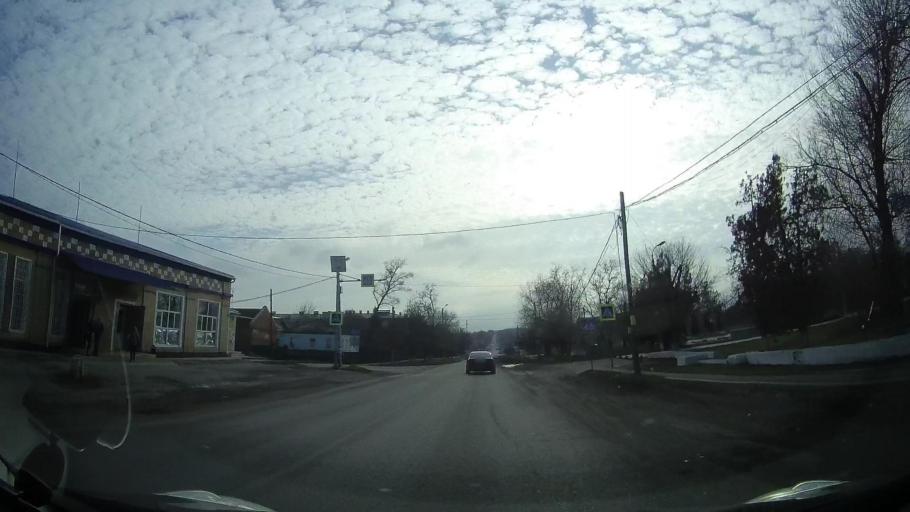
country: RU
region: Rostov
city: Mechetinskaya
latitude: 46.7671
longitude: 40.4548
